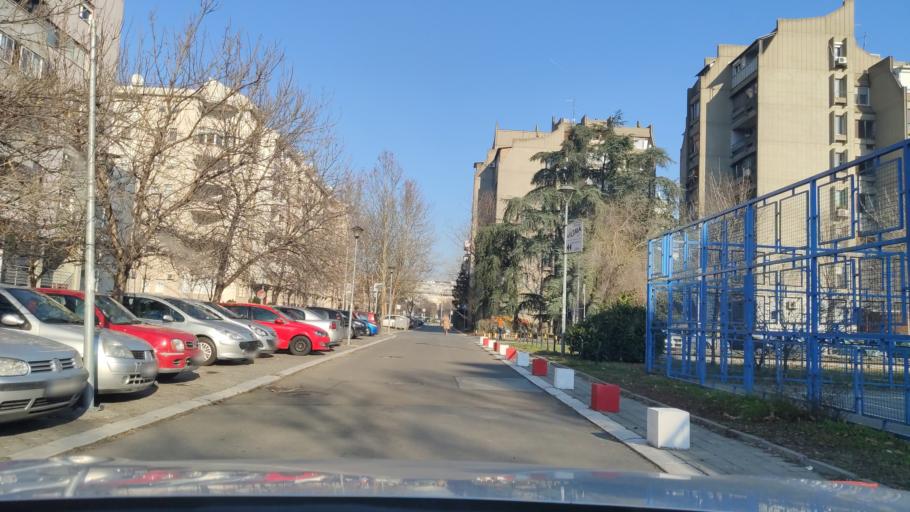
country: RS
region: Central Serbia
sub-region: Belgrade
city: Novi Beograd
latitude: 44.8115
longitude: 20.4268
